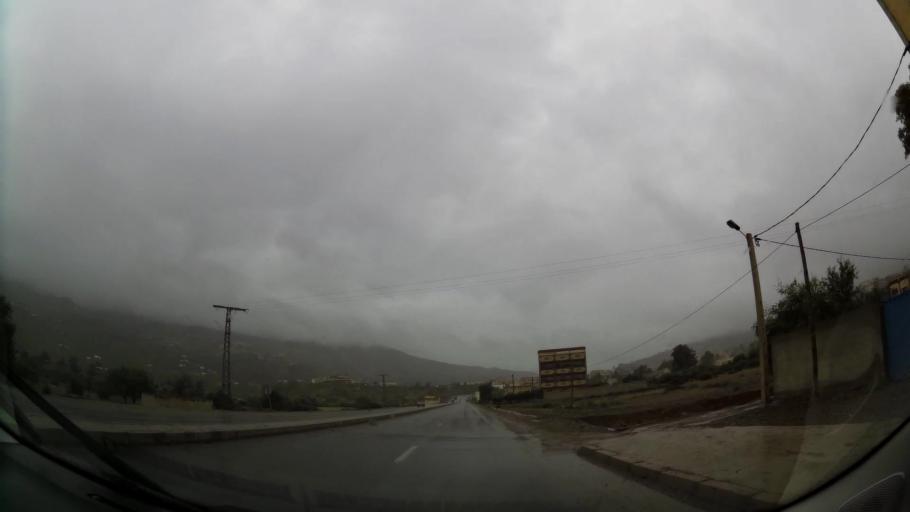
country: MA
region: Taza-Al Hoceima-Taounate
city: Imzourene
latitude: 35.0450
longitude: -3.8242
